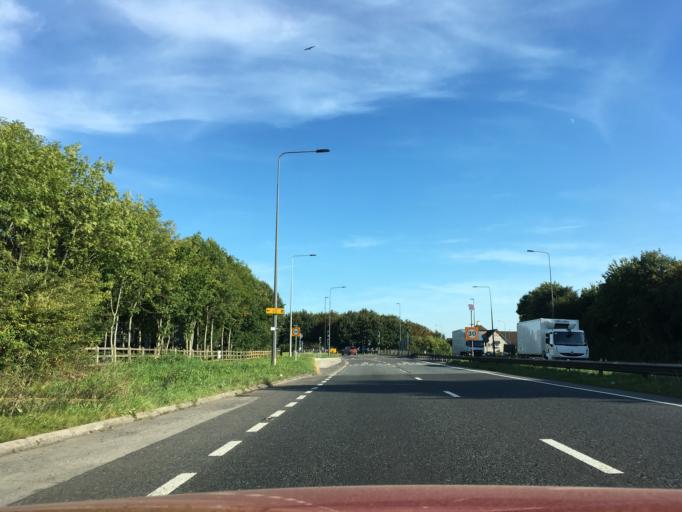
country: GB
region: England
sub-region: South Gloucestershire
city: Mangotsfield
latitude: 51.5006
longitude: -2.4820
